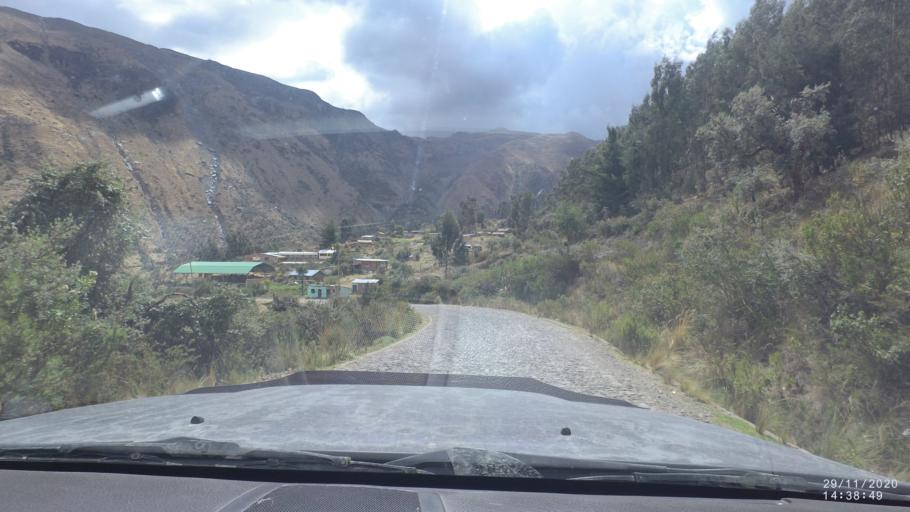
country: BO
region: Cochabamba
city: Sipe Sipe
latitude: -17.2725
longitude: -66.3285
